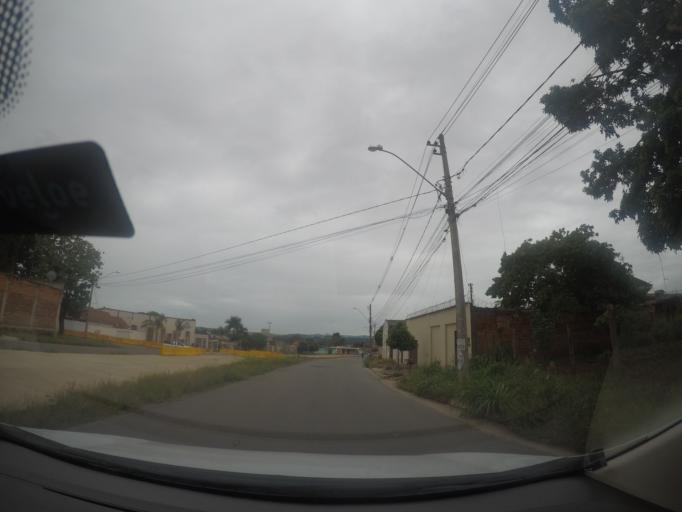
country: BR
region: Goias
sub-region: Goiania
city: Goiania
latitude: -16.6171
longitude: -49.2979
